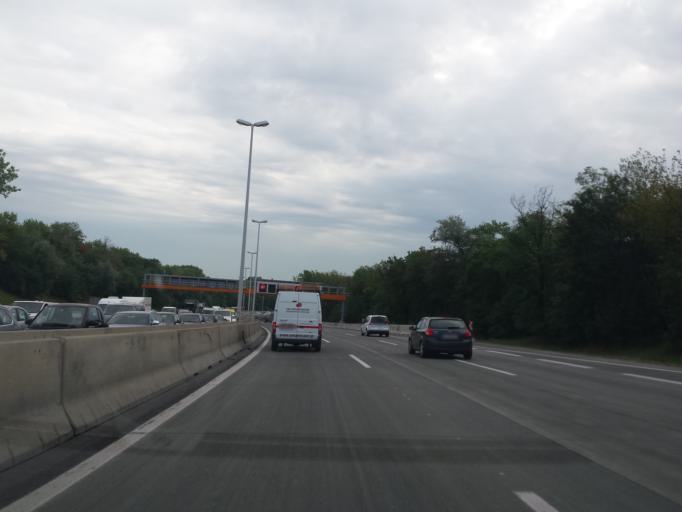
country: AT
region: Lower Austria
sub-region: Politischer Bezirk Wien-Umgebung
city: Leopoldsdorf
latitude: 48.1556
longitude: 16.3755
